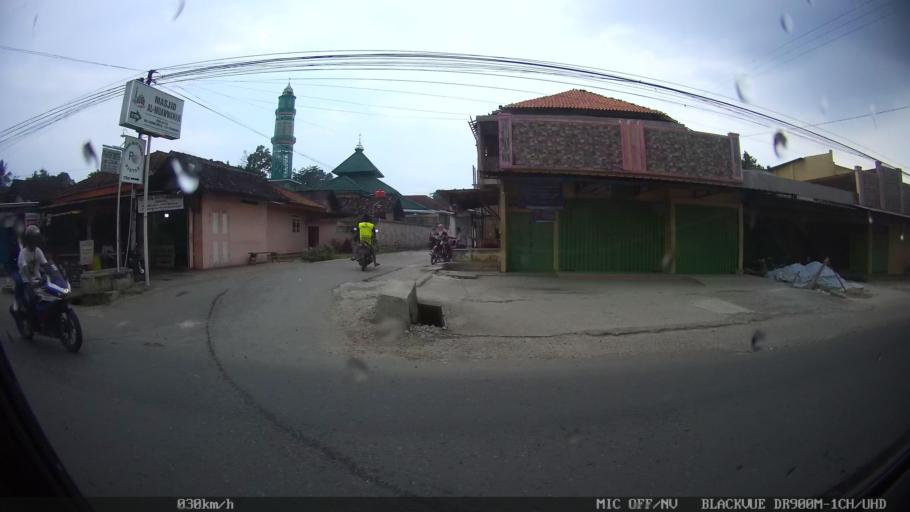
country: ID
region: Lampung
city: Gedongtataan
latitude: -5.3750
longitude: 105.1289
